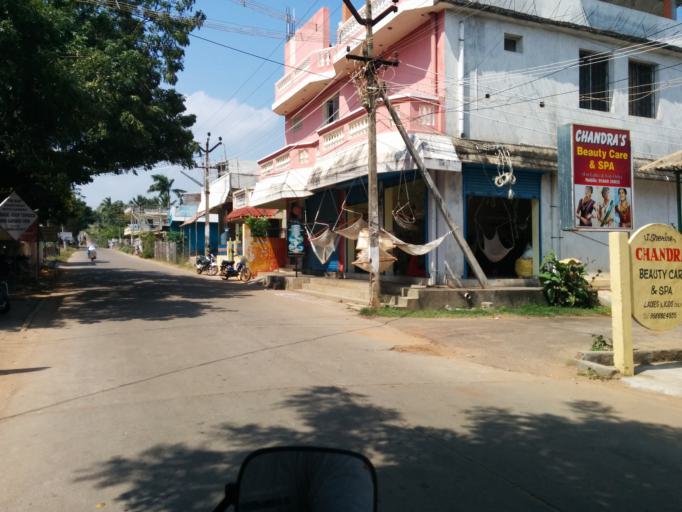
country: IN
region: Tamil Nadu
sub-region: Villupuram
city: Auroville
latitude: 11.9862
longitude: 79.8411
